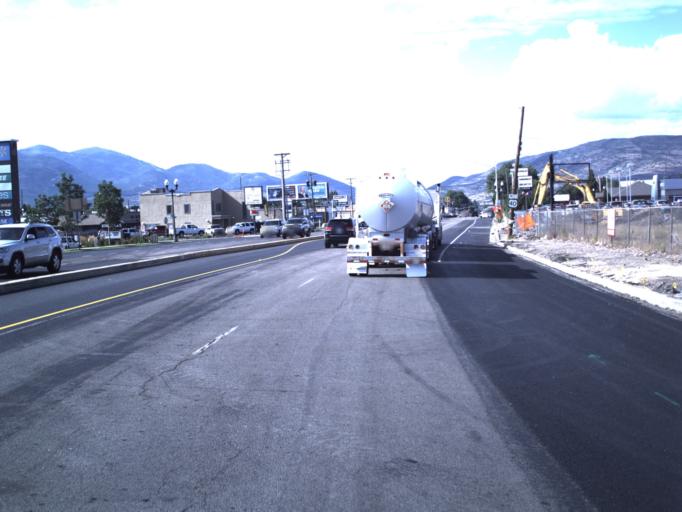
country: US
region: Utah
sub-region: Wasatch County
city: Heber
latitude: 40.4937
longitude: -111.4135
